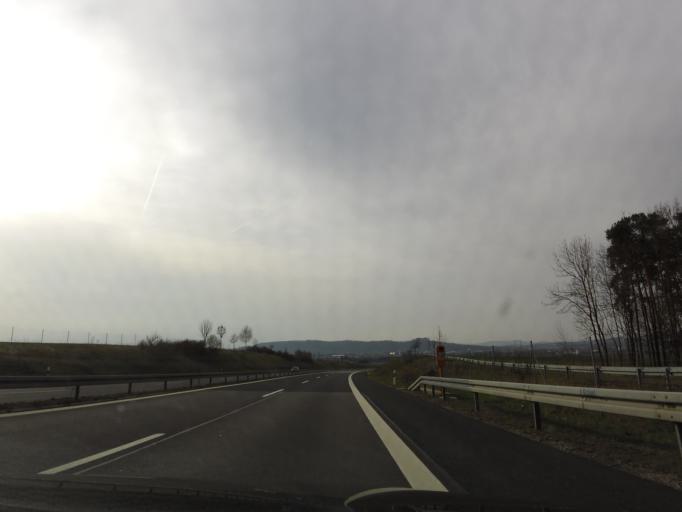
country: DE
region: Bavaria
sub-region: Upper Franconia
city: Lautertal
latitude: 50.3146
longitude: 10.9604
